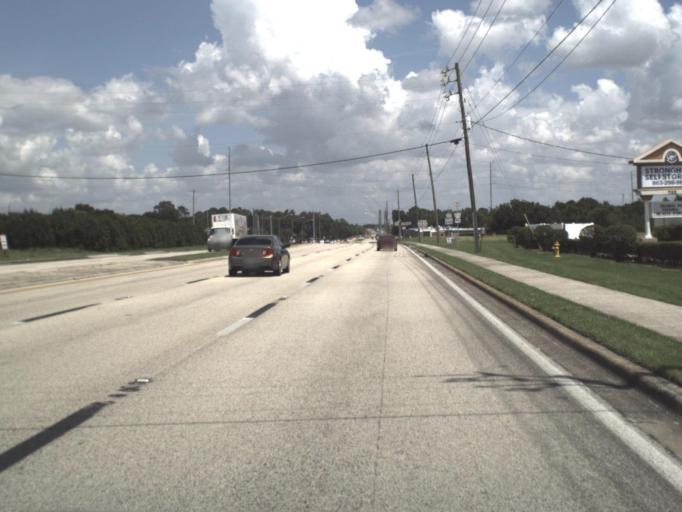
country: US
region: Florida
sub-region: Polk County
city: Eagle Lake
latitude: 27.9842
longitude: -81.7499
